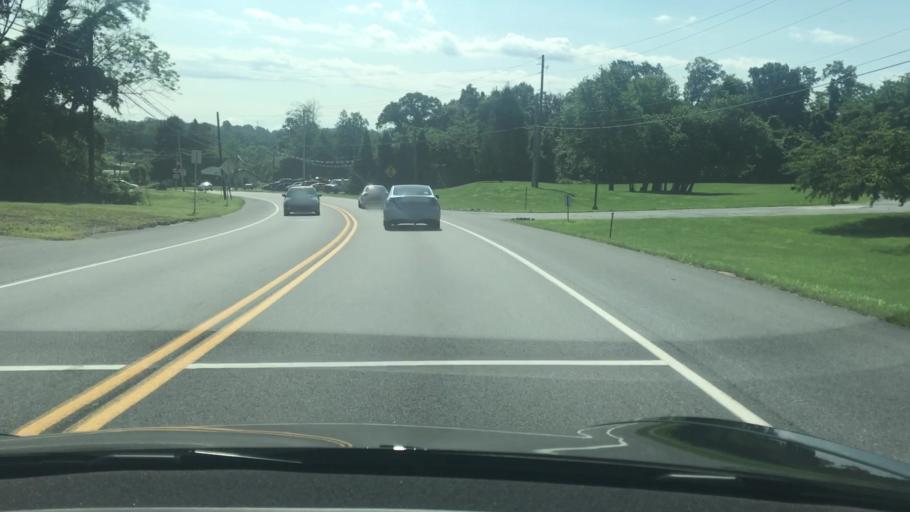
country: US
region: Pennsylvania
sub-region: York County
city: Valley Green
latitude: 40.1316
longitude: -76.8007
